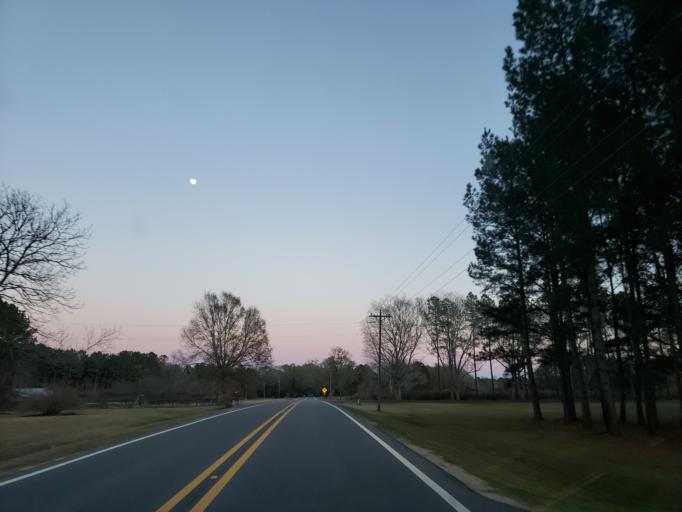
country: US
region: Mississippi
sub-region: Jones County
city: Ellisville
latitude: 31.5797
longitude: -89.2552
